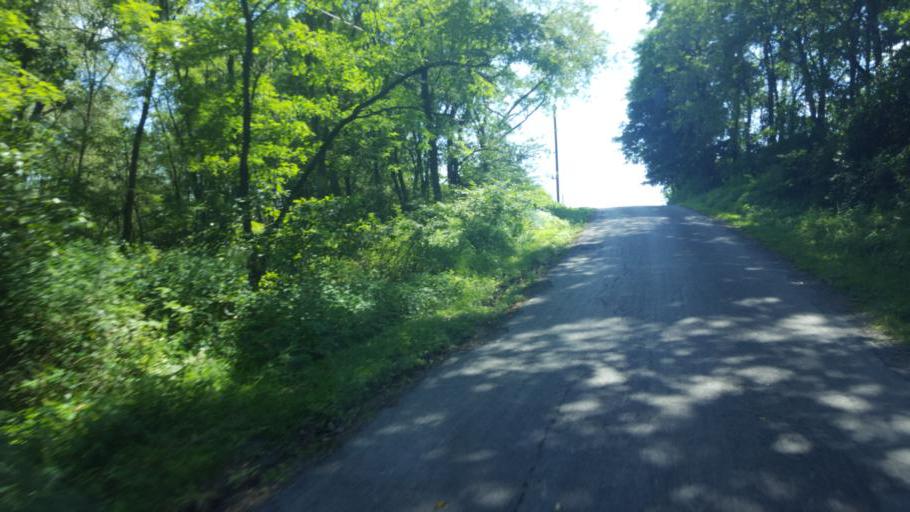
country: US
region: Pennsylvania
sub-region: Clarion County
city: Knox
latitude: 41.1233
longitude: -79.5485
